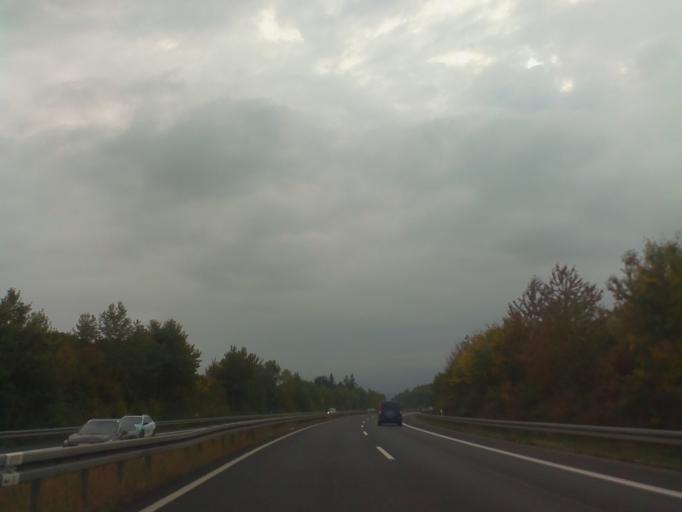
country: DE
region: Hesse
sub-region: Regierungsbezirk Darmstadt
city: Schluchtern
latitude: 50.3488
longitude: 9.5008
